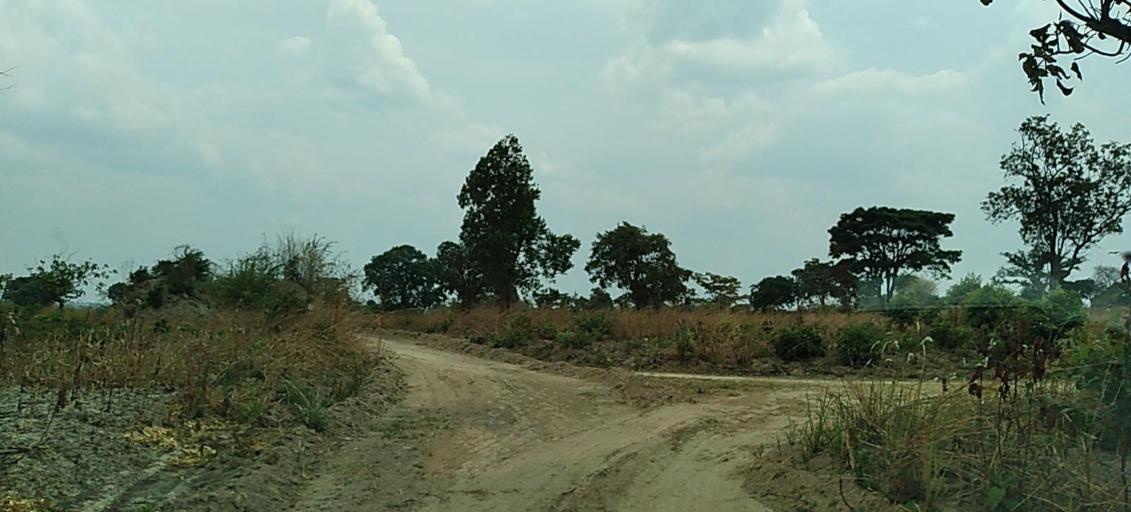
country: ZM
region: Copperbelt
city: Chililabombwe
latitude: -12.3535
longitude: 27.7976
